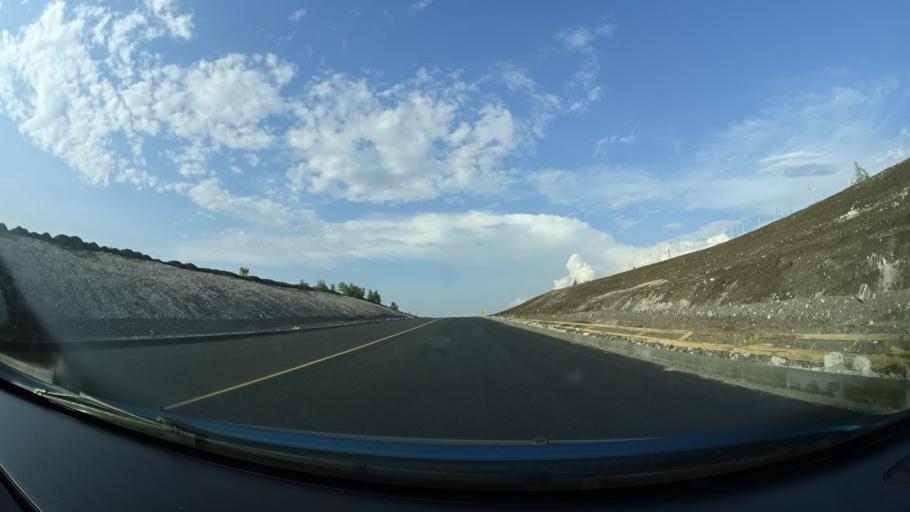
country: RU
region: Samara
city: Sukhodol
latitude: 53.7320
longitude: 50.8426
